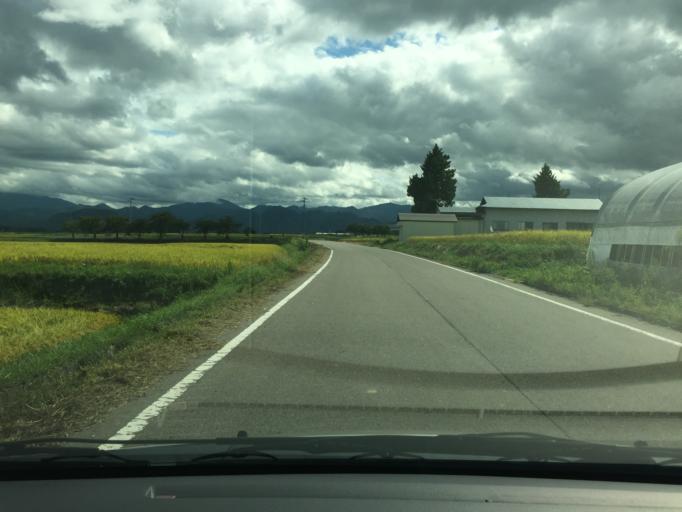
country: JP
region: Fukushima
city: Kitakata
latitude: 37.4769
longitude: 139.8193
